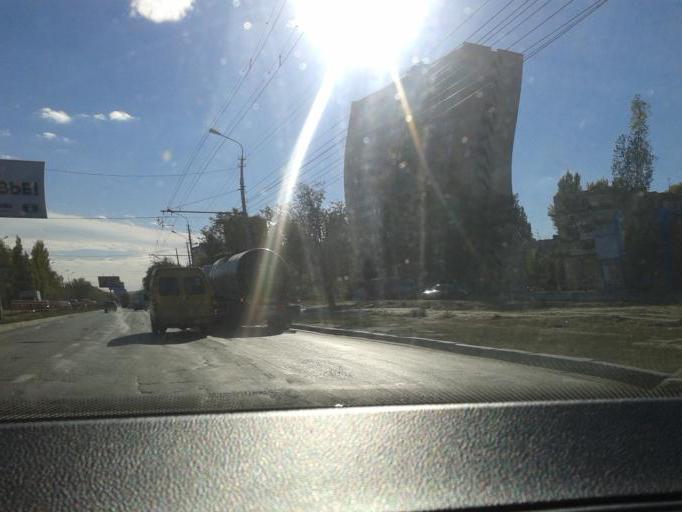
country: RU
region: Volgograd
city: Volgograd
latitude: 48.6233
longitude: 44.4254
